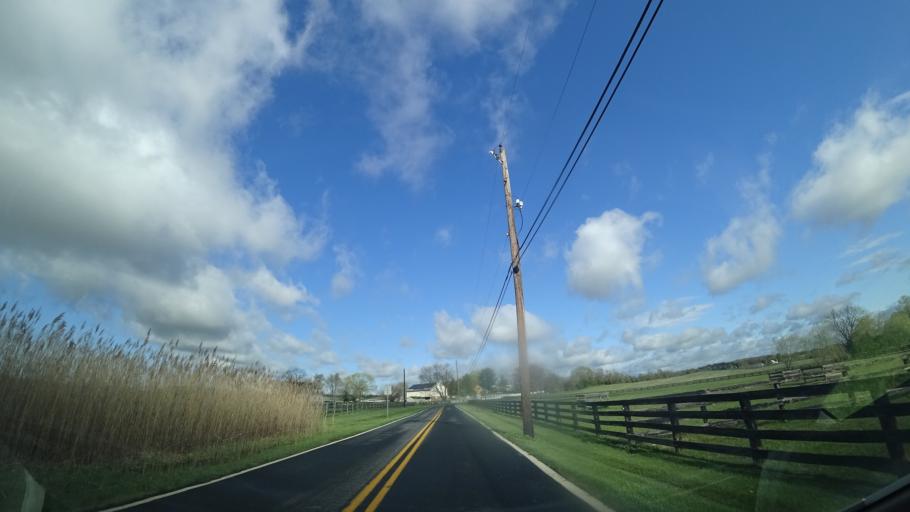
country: US
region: Virginia
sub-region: Loudoun County
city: Lowes Island
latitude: 39.1065
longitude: -77.3780
